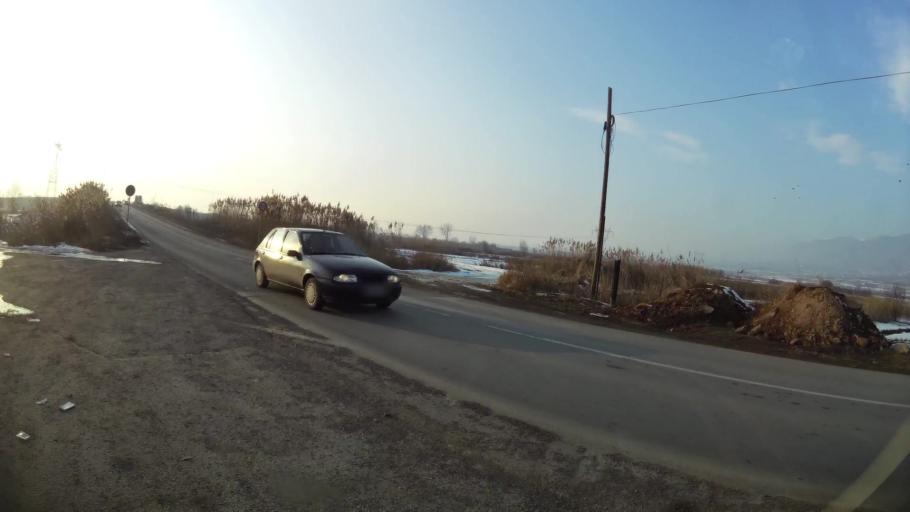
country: MK
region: Aracinovo
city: Arachinovo
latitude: 42.0192
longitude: 21.5370
